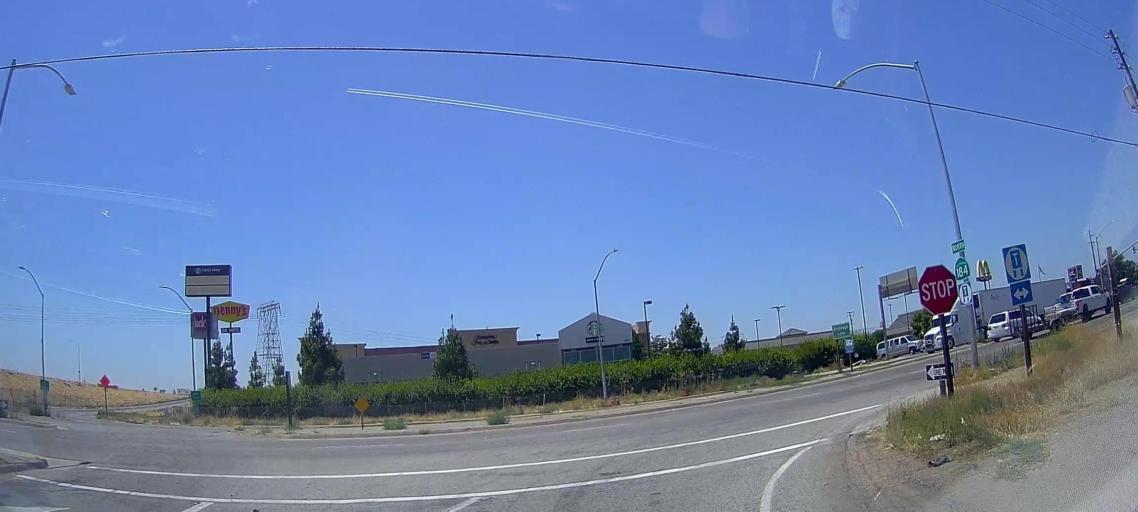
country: US
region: California
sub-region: Kern County
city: Lamont
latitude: 35.3537
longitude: -118.9140
